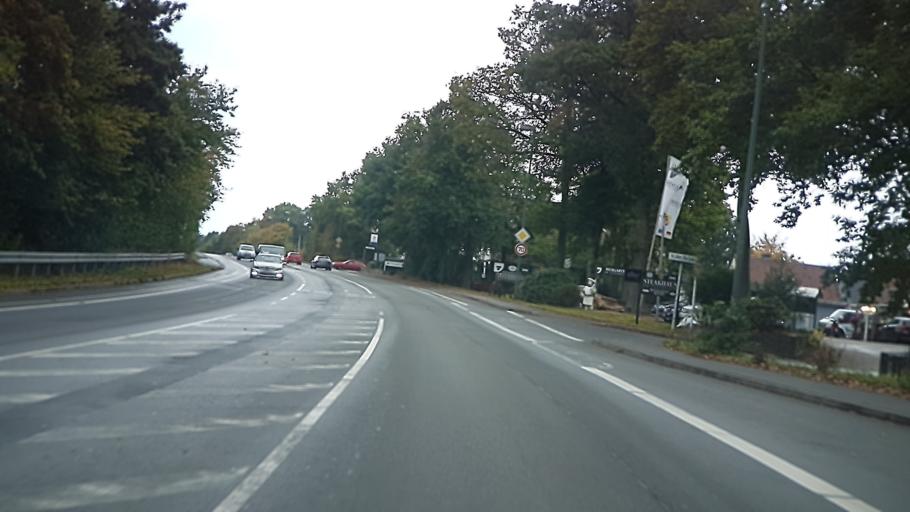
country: DE
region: North Rhine-Westphalia
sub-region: Regierungsbezirk Arnsberg
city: Luedenscheid
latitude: 51.1974
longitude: 7.6668
